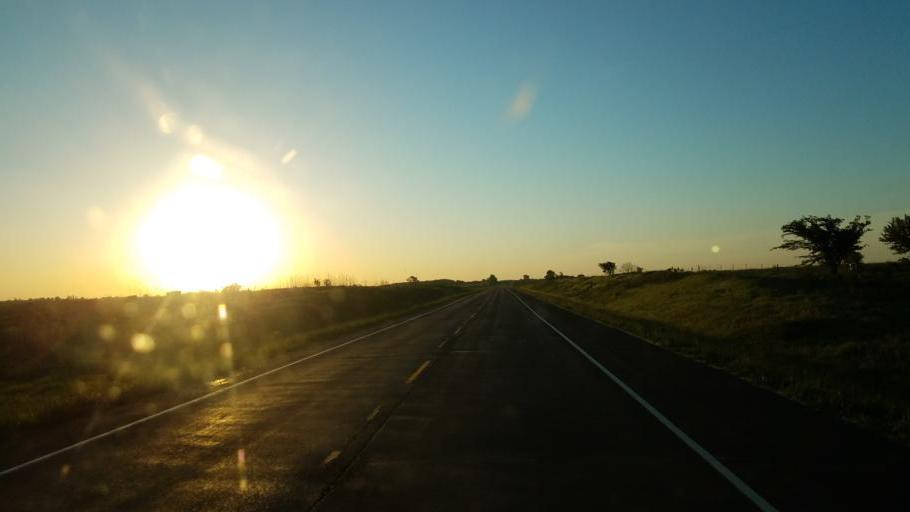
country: US
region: Missouri
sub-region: Schuyler County
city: Lancaster
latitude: 40.4926
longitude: -92.5728
